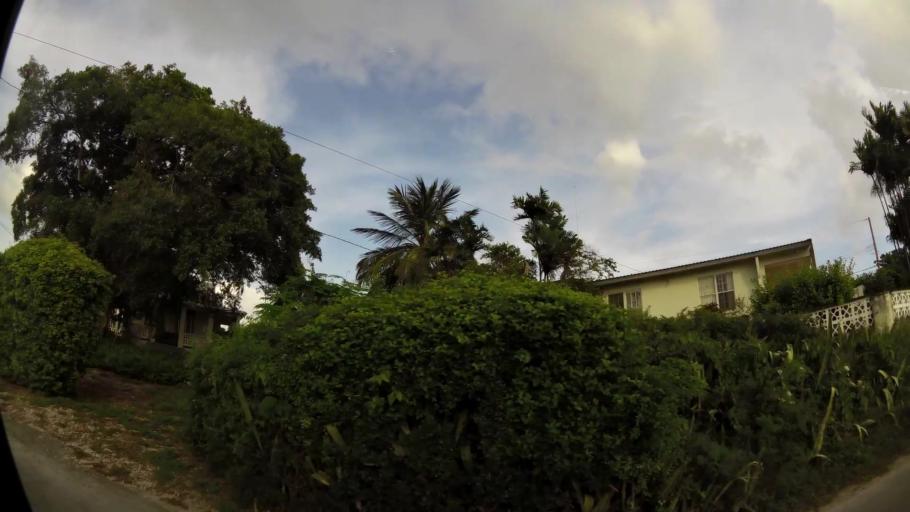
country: BB
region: Christ Church
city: Oistins
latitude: 13.0546
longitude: -59.5355
